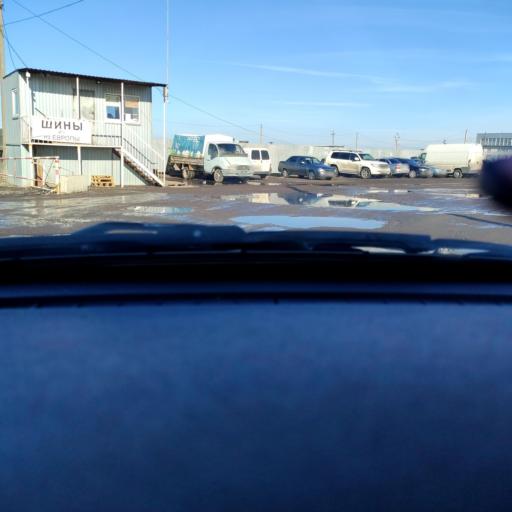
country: RU
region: Voronezj
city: Novaya Usman'
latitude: 51.6411
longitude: 39.3234
